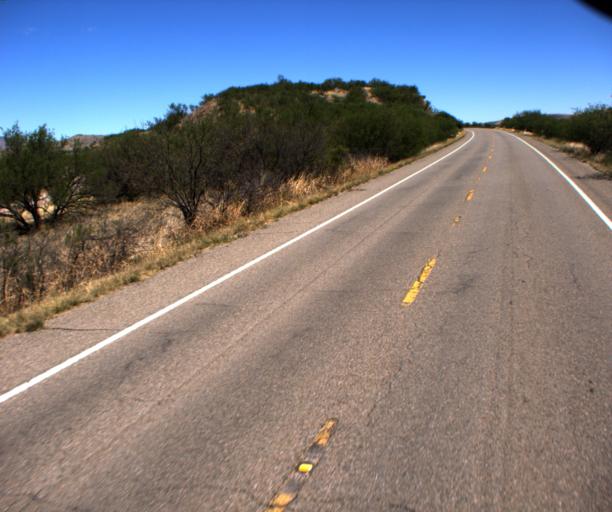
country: US
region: Arizona
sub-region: Santa Cruz County
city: Rio Rico
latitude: 31.5992
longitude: -110.7230
